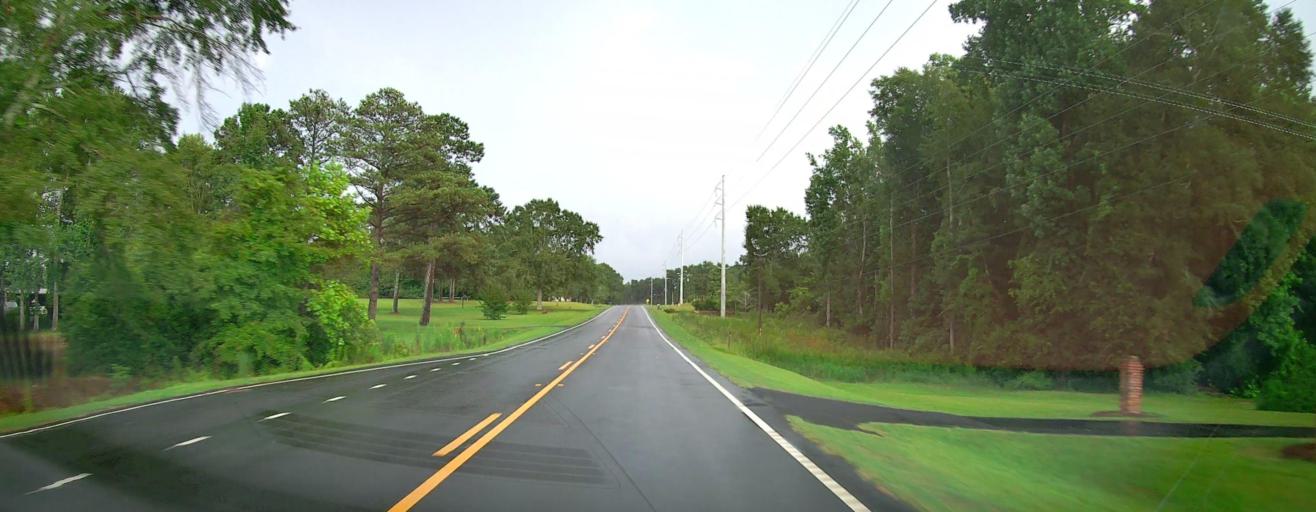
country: US
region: Georgia
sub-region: Twiggs County
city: Jeffersonville
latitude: 32.5876
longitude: -83.2241
